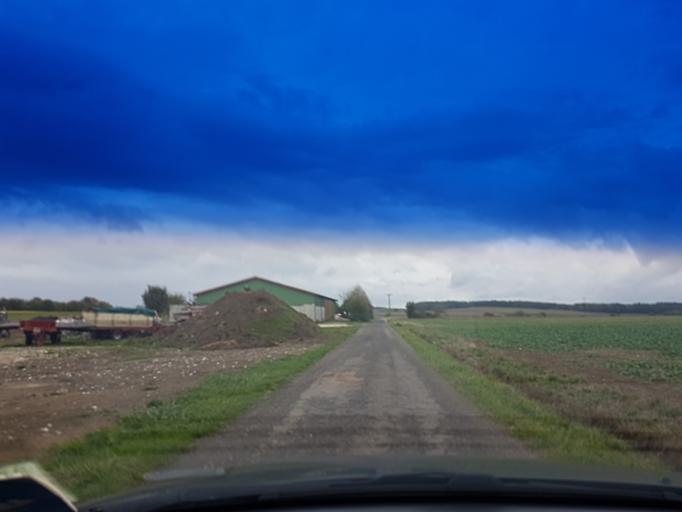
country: DE
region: Bavaria
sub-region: Upper Franconia
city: Schesslitz
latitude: 49.9997
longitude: 11.0251
